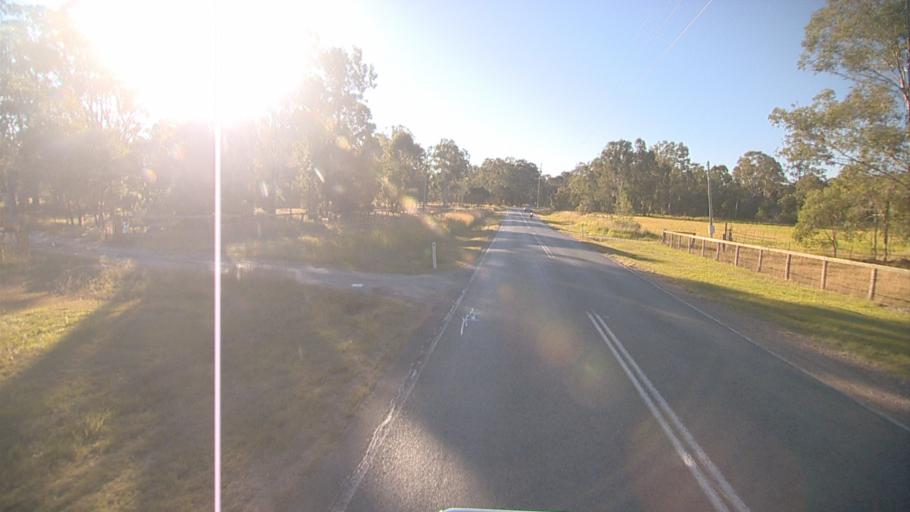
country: AU
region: Queensland
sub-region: Logan
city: Chambers Flat
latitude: -27.7421
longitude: 153.0874
